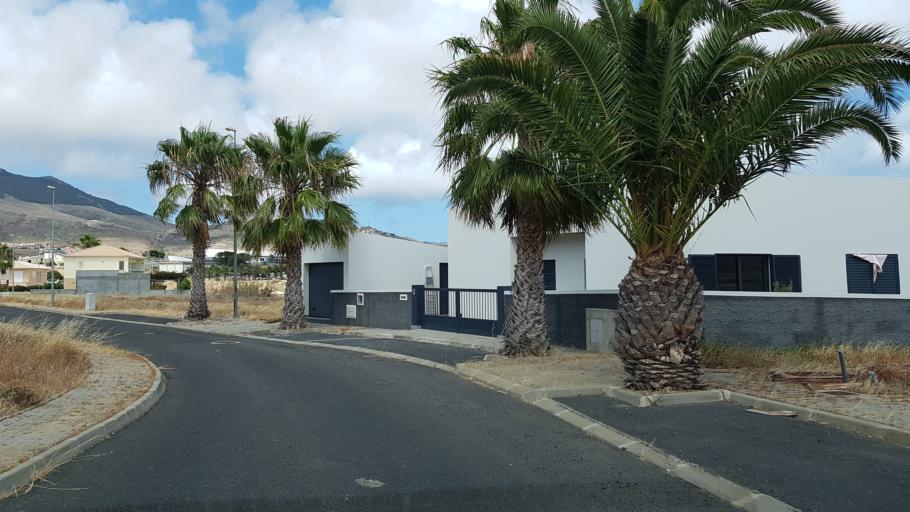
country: PT
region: Madeira
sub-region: Porto Santo
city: Vila de Porto Santo
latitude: 33.0578
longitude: -16.3436
